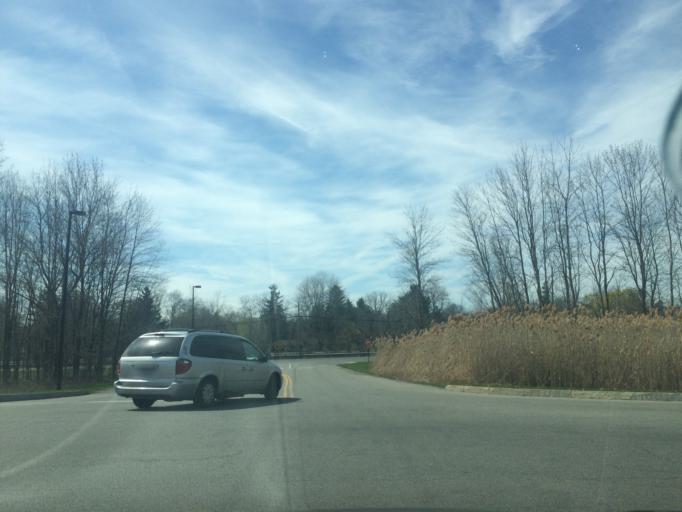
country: US
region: New York
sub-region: Monroe County
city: Scottsville
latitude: 43.0853
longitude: -77.6847
